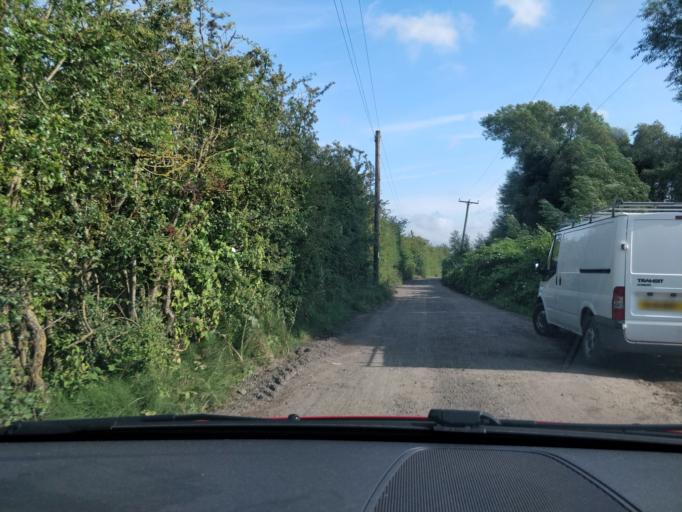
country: GB
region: England
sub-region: Sefton
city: Southport
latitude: 53.6517
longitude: -2.9565
